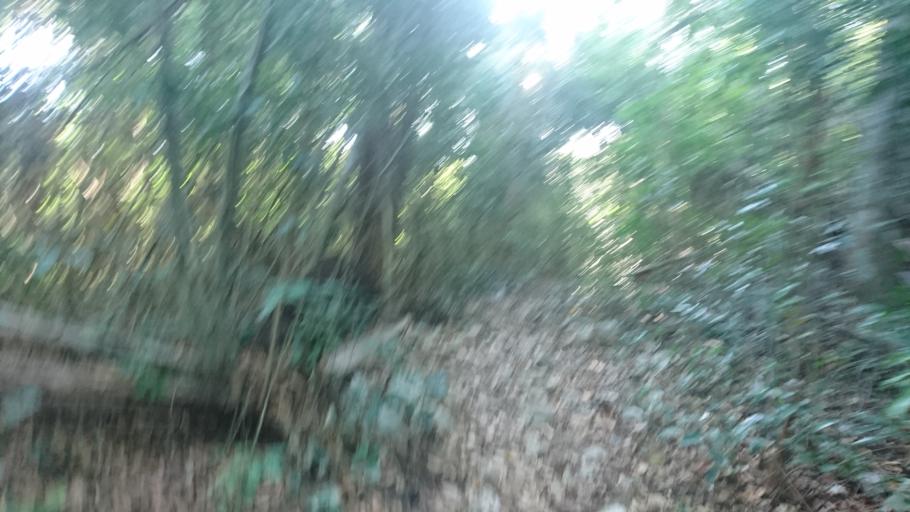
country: CU
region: Artemisa
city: Soroa
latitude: 22.8317
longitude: -82.9191
